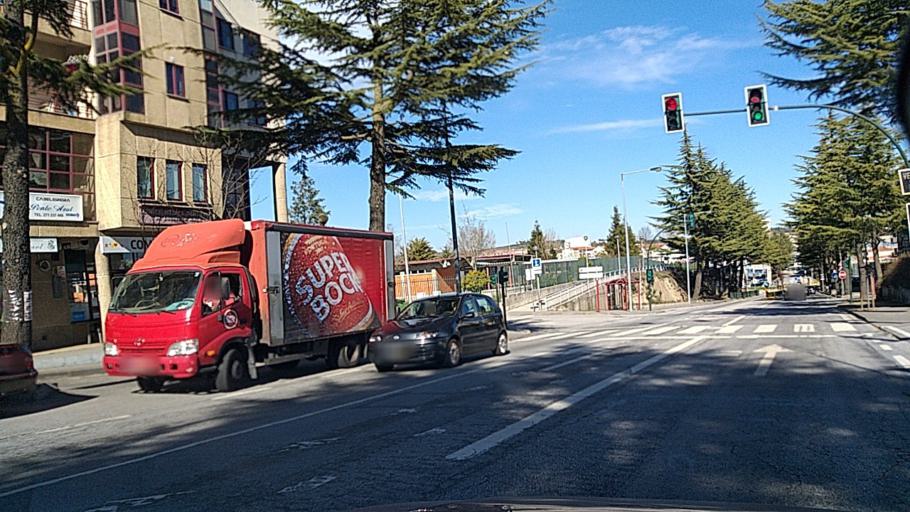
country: PT
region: Guarda
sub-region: Guarda
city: Guarda
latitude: 40.5477
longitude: -7.2508
